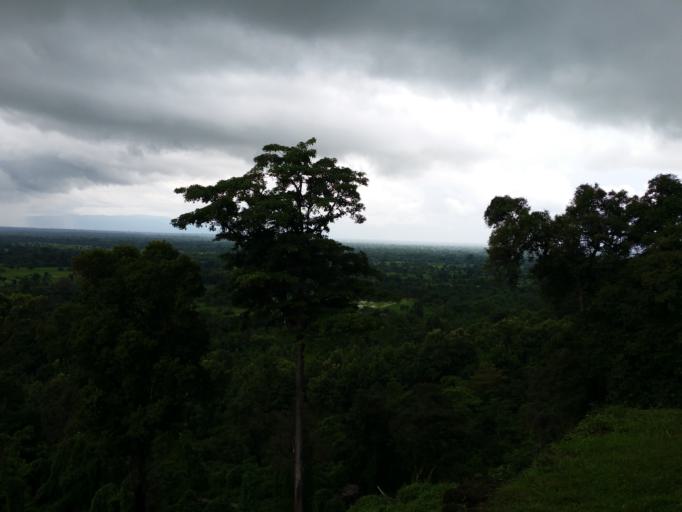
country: LA
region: Champasak
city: Champasak
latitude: 14.8485
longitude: 105.8148
